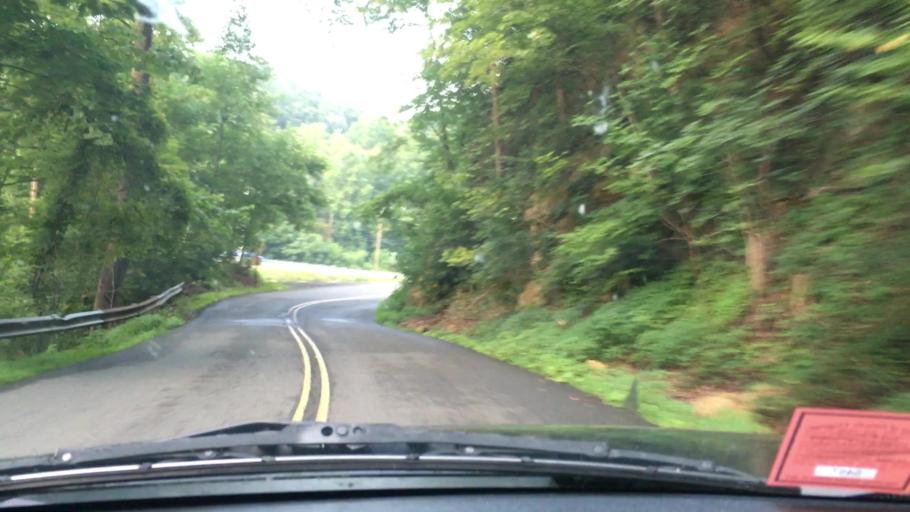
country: US
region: Virginia
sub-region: Pulaski County
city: Pulaski
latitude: 37.0413
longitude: -80.7420
